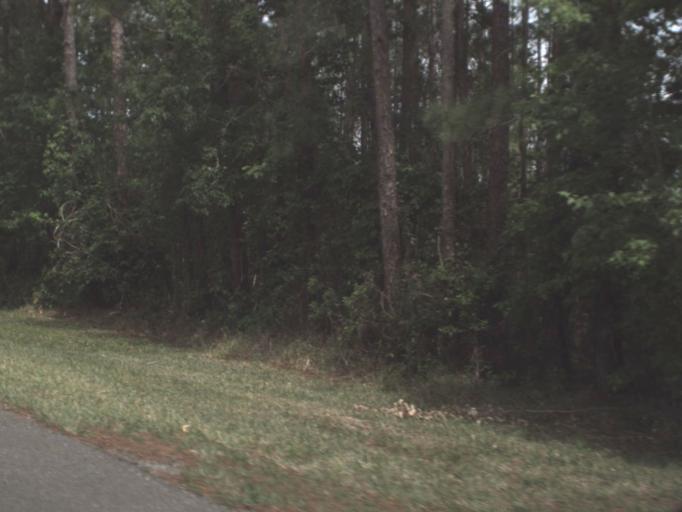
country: US
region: Florida
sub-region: Volusia County
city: Pierson
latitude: 29.2762
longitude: -81.3345
